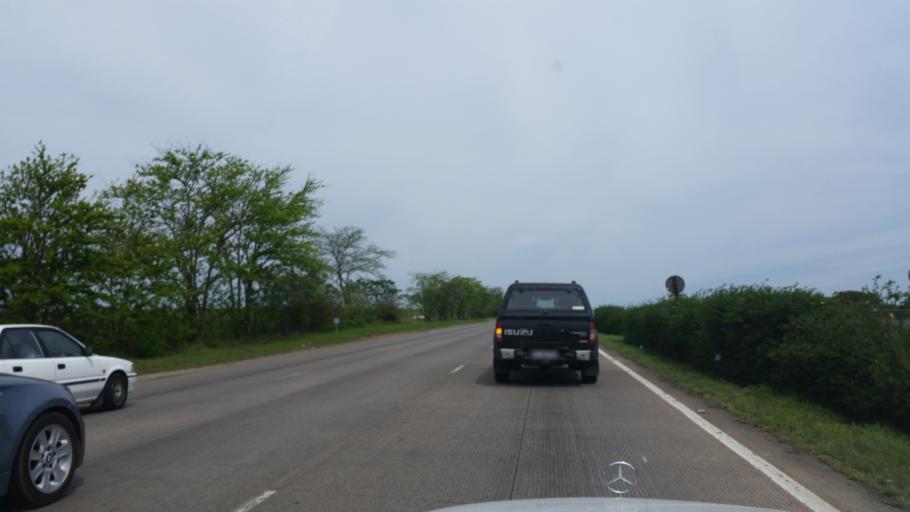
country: ZA
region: KwaZulu-Natal
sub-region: uMgungundlovu District Municipality
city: Camperdown
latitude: -29.6777
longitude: 30.4704
